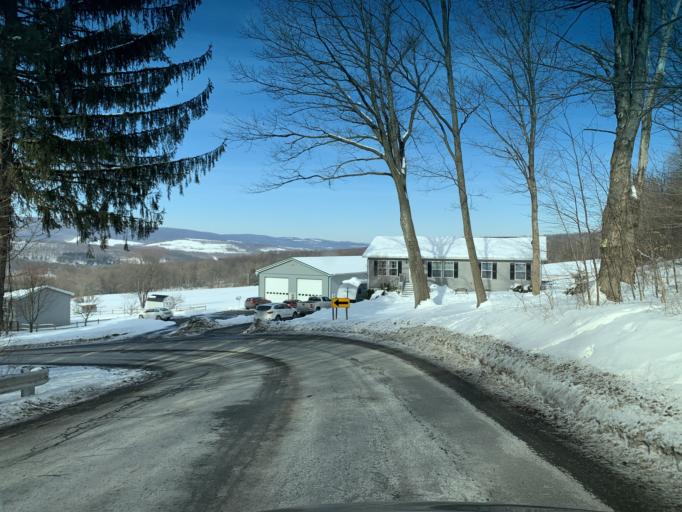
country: US
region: Maryland
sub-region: Allegany County
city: Frostburg
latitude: 39.6706
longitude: -78.8912
